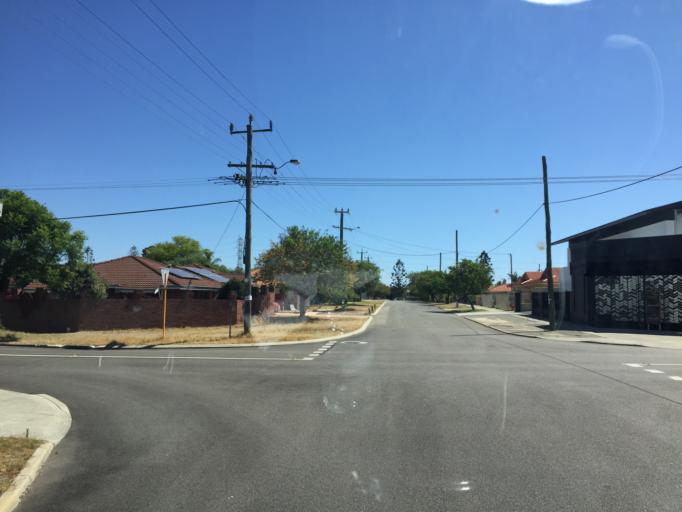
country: AU
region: Western Australia
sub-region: Victoria Park
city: Victoria Park
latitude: -31.9809
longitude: 115.9144
